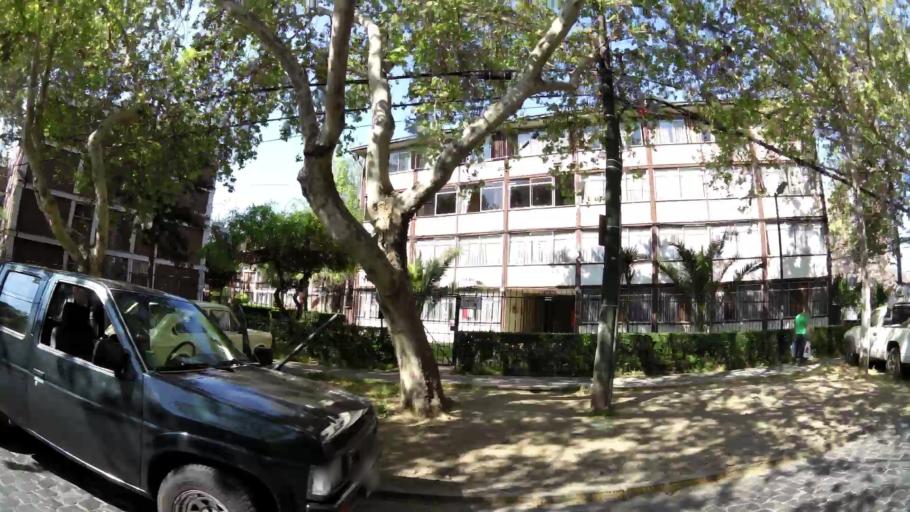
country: CL
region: Santiago Metropolitan
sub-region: Provincia de Santiago
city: Santiago
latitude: -33.4543
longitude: -70.6250
